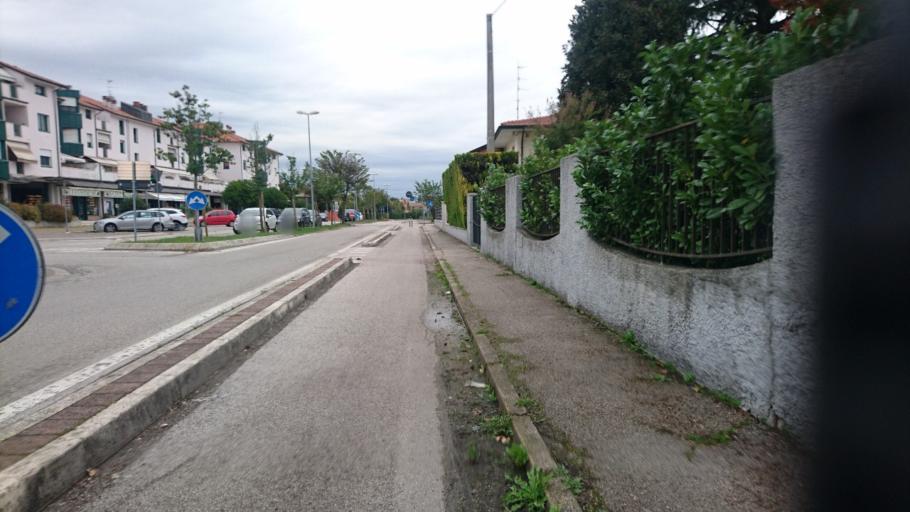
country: IT
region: Veneto
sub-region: Provincia di Vicenza
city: Creazzo
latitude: 45.5311
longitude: 11.4797
